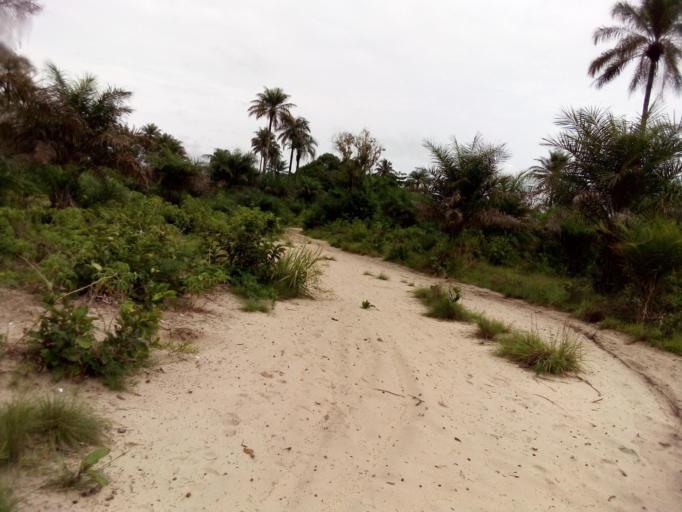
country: SL
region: Southern Province
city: Bonthe
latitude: 7.5215
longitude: -12.5762
